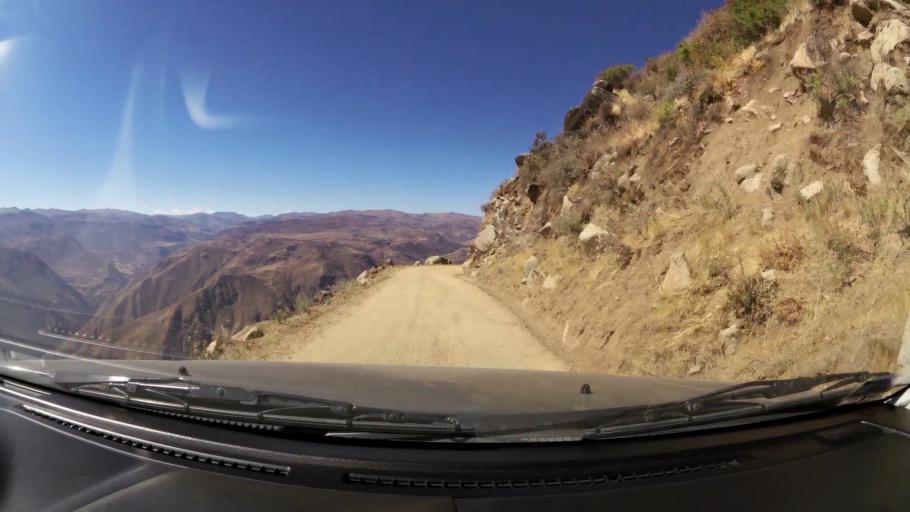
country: PE
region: Huancavelica
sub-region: Huaytara
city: Quito-Arma
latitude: -13.6231
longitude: -75.3542
